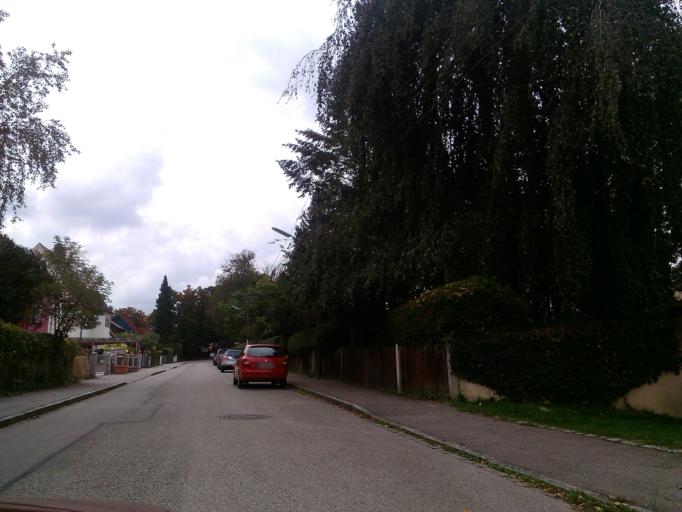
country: DE
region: Bavaria
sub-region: Upper Bavaria
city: Grafelfing
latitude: 48.1167
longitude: 11.4260
